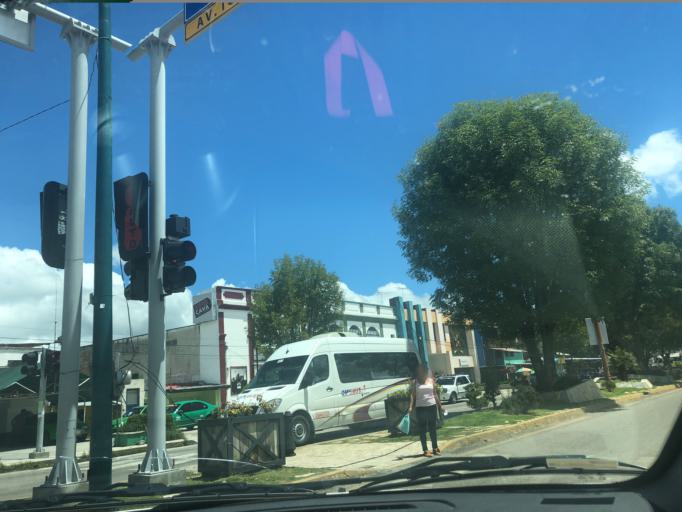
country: MX
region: Chiapas
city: San Cristobal de las Casas
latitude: 16.7303
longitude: -92.6403
